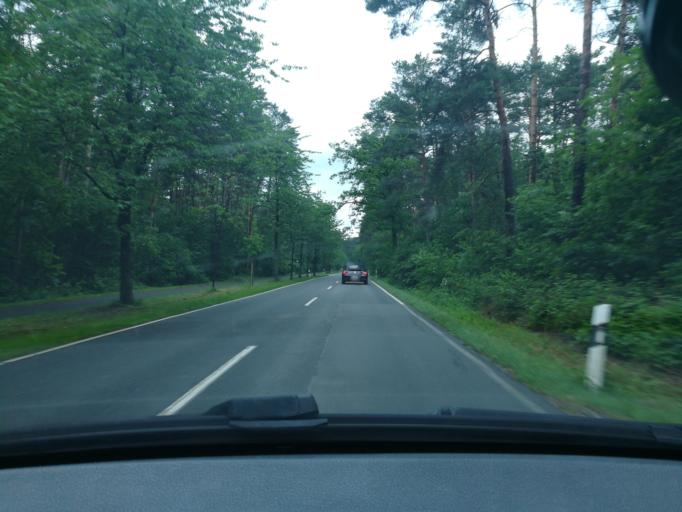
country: DE
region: North Rhine-Westphalia
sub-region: Regierungsbezirk Detmold
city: Oerlinghausen
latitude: 51.9202
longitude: 8.6555
